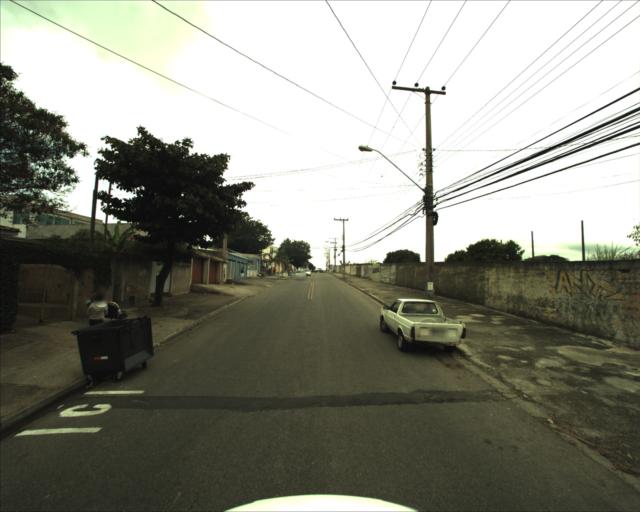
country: BR
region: Sao Paulo
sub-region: Sorocaba
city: Sorocaba
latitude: -23.5153
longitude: -47.4379
